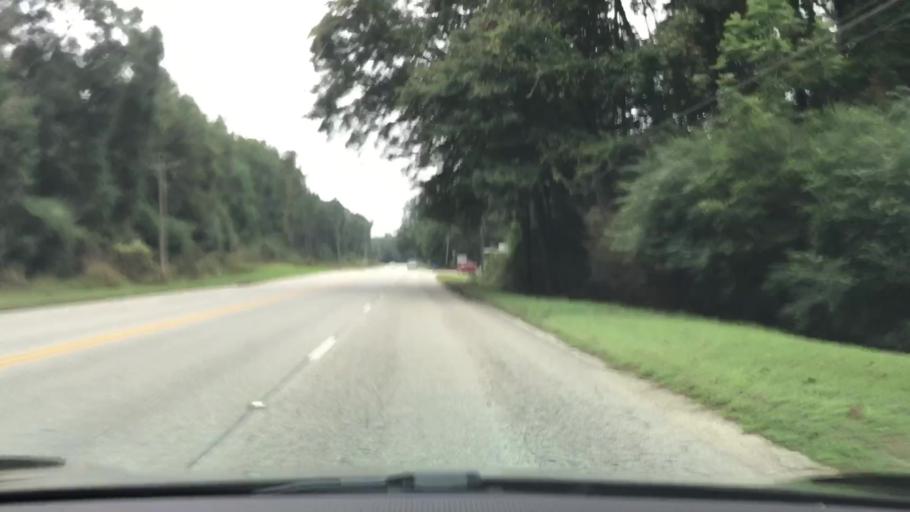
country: US
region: Alabama
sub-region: Coffee County
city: Elba
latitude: 31.4488
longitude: -86.0708
